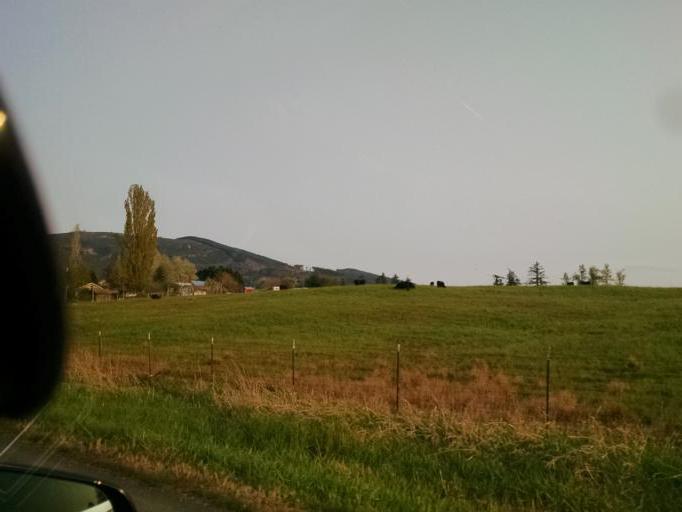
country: US
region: Washington
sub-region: Whatcom County
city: Geneva
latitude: 48.8038
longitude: -122.3580
